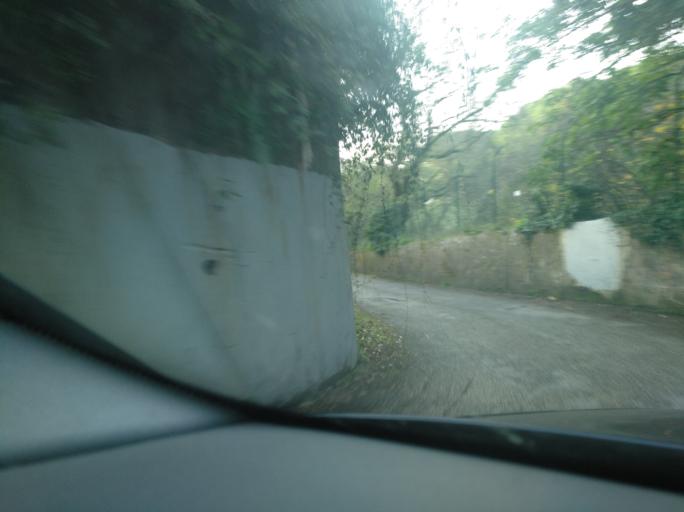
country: PT
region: Lisbon
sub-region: Odivelas
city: Olival do Basto
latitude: 38.7748
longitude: -9.1698
